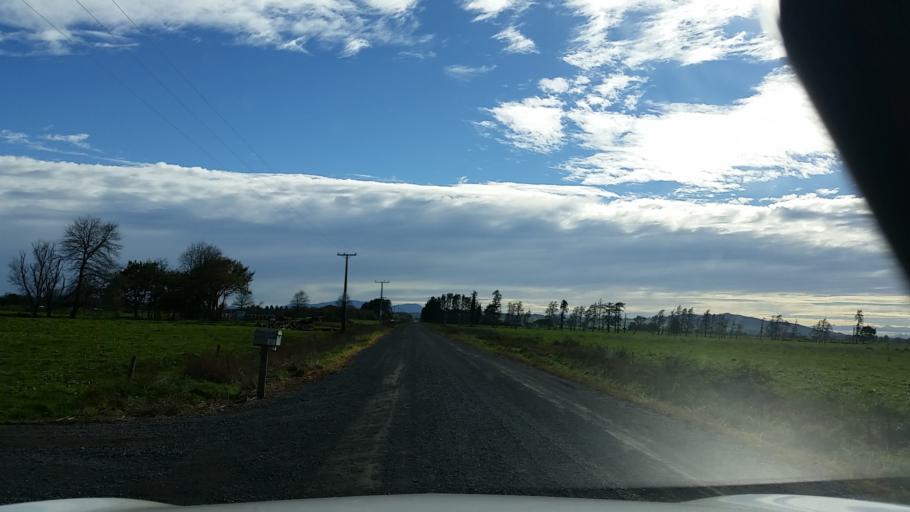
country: NZ
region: Waikato
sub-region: Hamilton City
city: Hamilton
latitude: -37.6647
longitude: 175.4385
